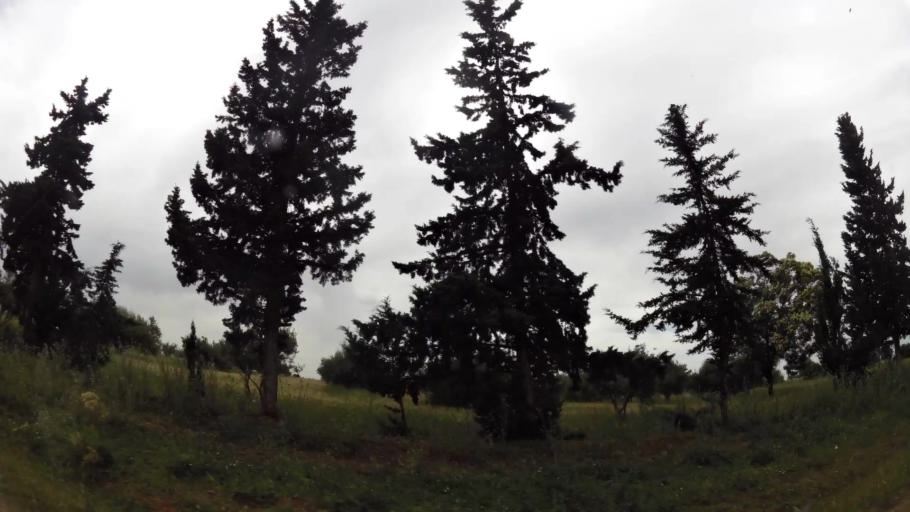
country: MA
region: Rabat-Sale-Zemmour-Zaer
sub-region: Khemisset
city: Tiflet
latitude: 33.8309
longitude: -6.2718
